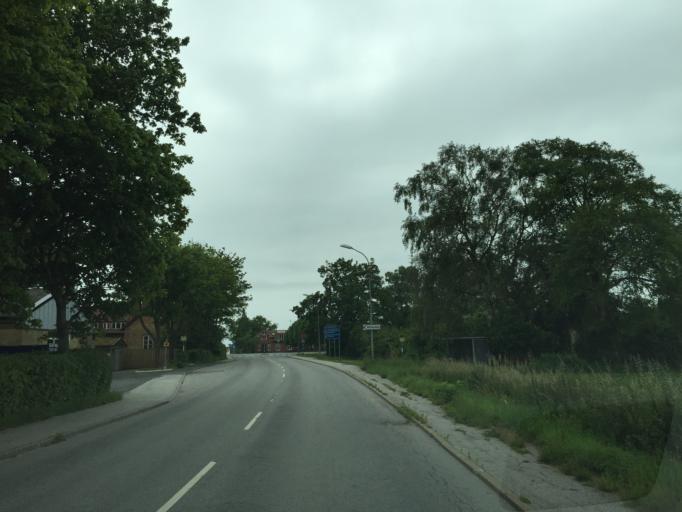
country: SE
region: Skane
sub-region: Ystads Kommun
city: Kopingebro
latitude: 55.4296
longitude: 14.1130
